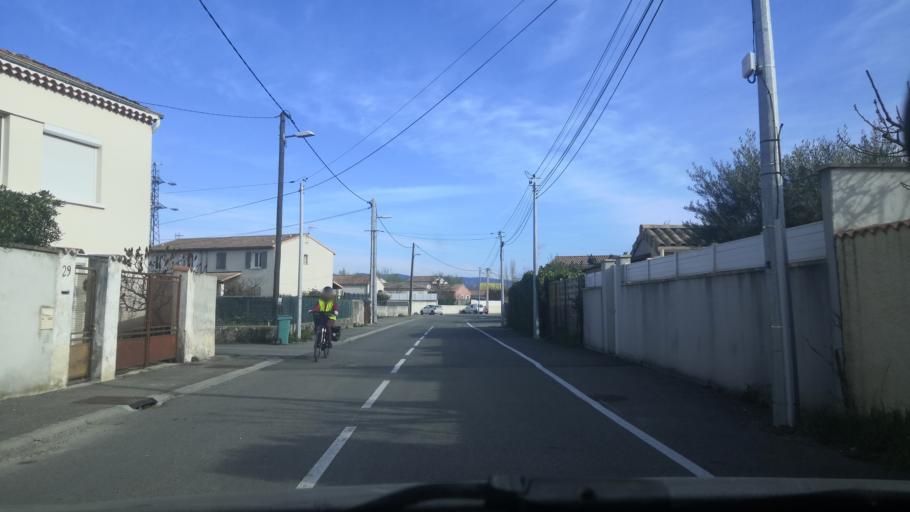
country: FR
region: Rhone-Alpes
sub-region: Departement de la Drome
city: Montelimar
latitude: 44.5673
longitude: 4.7439
